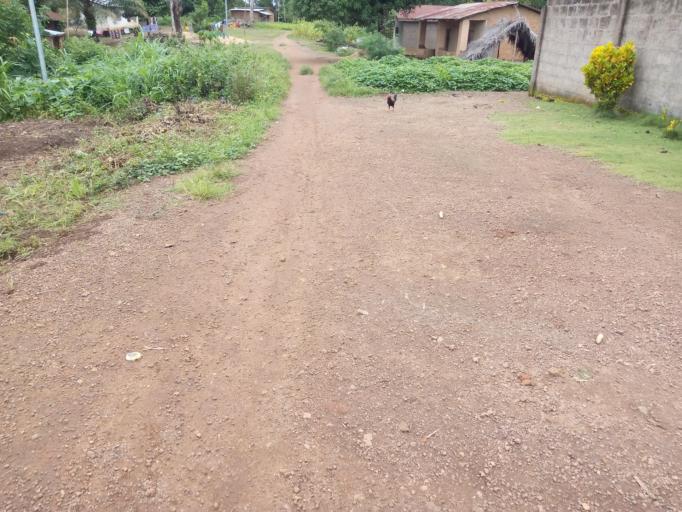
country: SL
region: Eastern Province
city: Buedu
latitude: 8.4539
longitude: -10.3315
